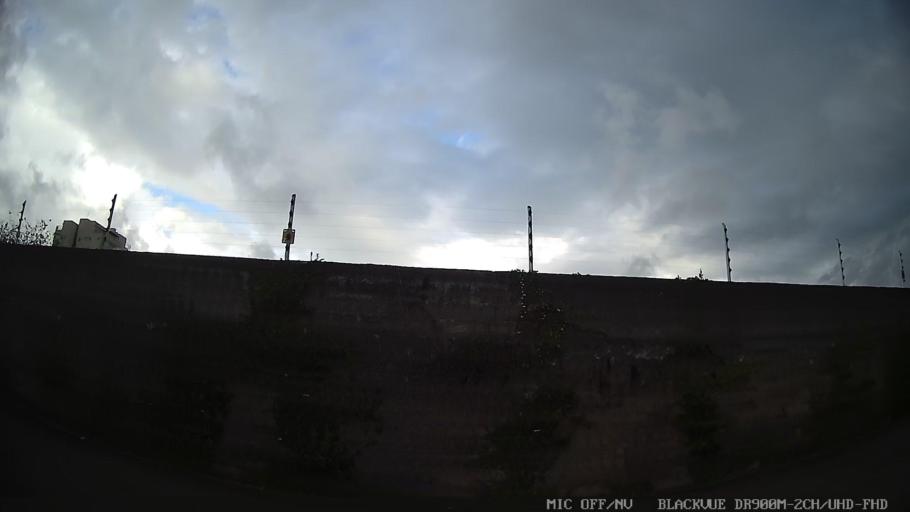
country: BR
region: Sao Paulo
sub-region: Caraguatatuba
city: Caraguatatuba
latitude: -23.6358
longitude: -45.4265
